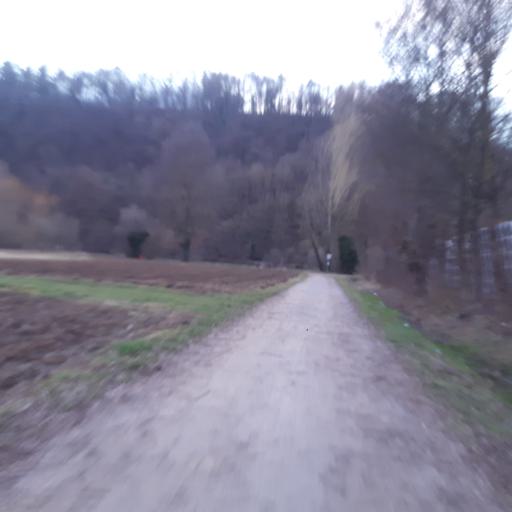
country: DE
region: Baden-Wuerttemberg
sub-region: Regierungsbezirk Stuttgart
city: Mundelsheim
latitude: 48.9938
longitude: 9.2044
